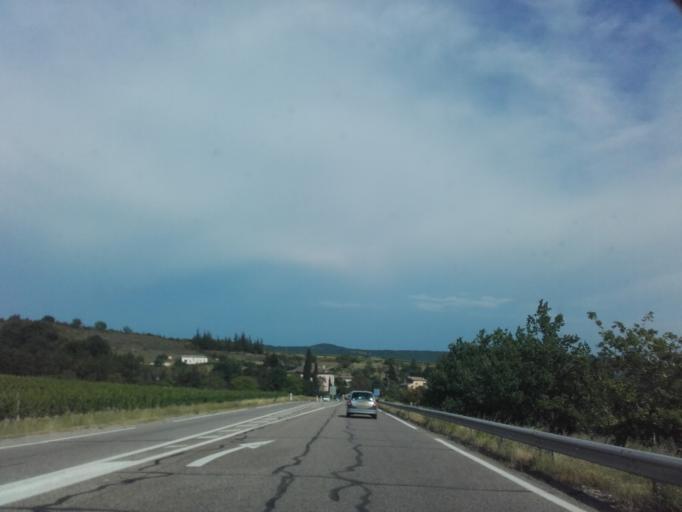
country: FR
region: Rhone-Alpes
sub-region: Departement de l'Ardeche
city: Alba-la-Romaine
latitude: 44.5722
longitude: 4.5840
